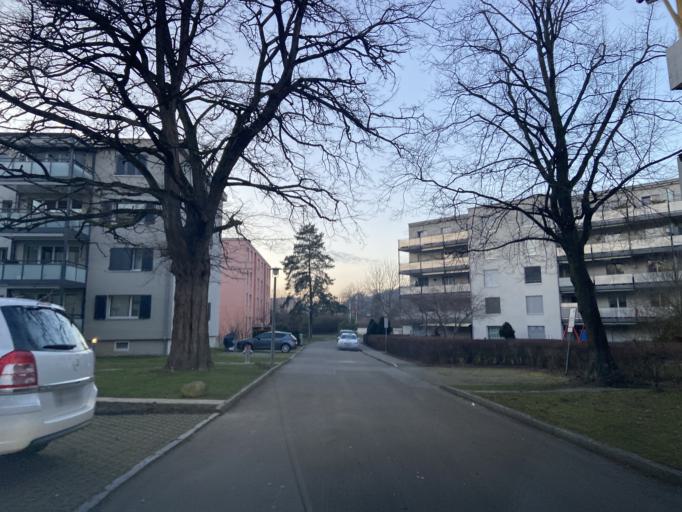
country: CH
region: Zurich
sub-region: Bezirk Winterthur
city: Wuelflingen (Kreis 6) / Lindenplatz
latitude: 47.5120
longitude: 8.6906
